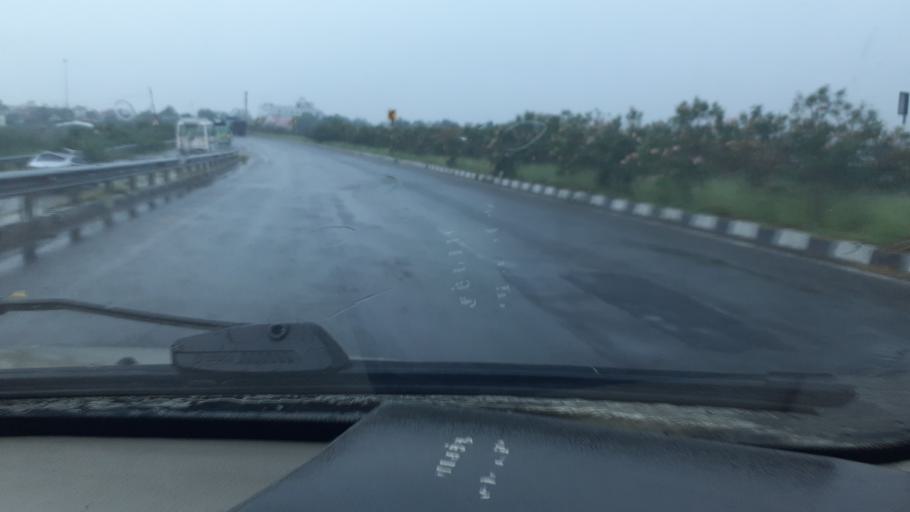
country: IN
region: Tamil Nadu
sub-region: Virudhunagar
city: Sattur
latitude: 9.3779
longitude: 77.9127
